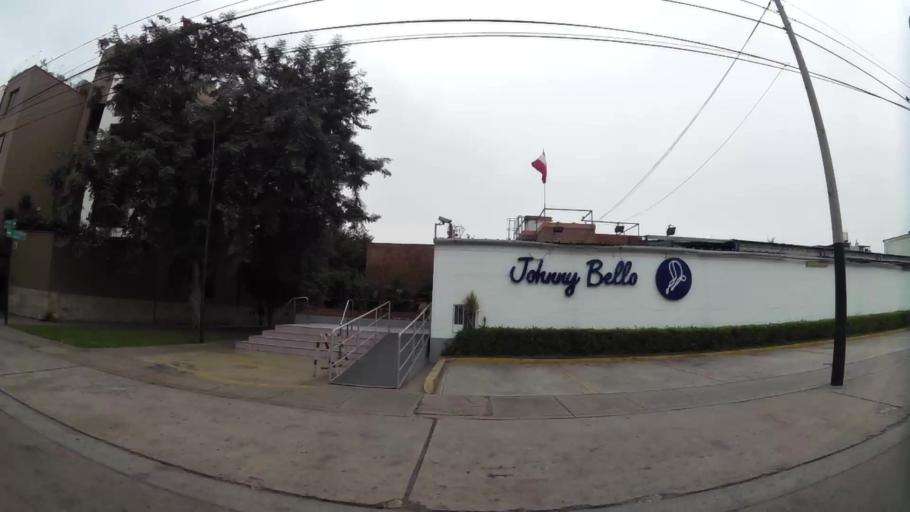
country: PE
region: Lima
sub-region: Lima
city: Surco
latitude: -12.1192
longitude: -76.9873
